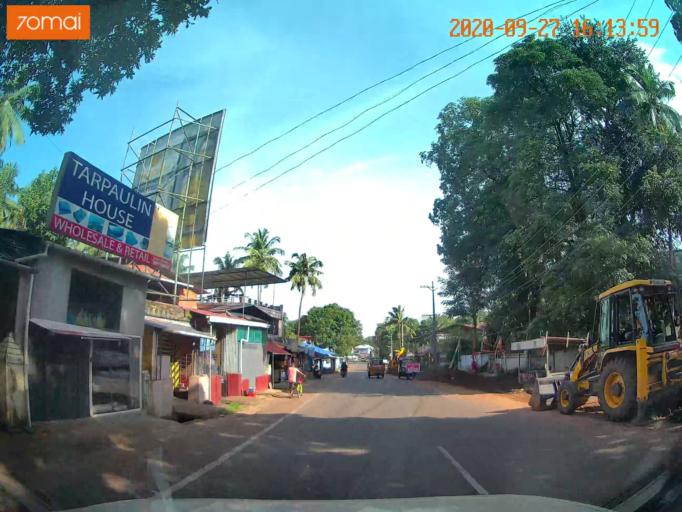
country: IN
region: Kerala
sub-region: Thrissur District
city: Trichur
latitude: 10.4663
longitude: 76.2460
